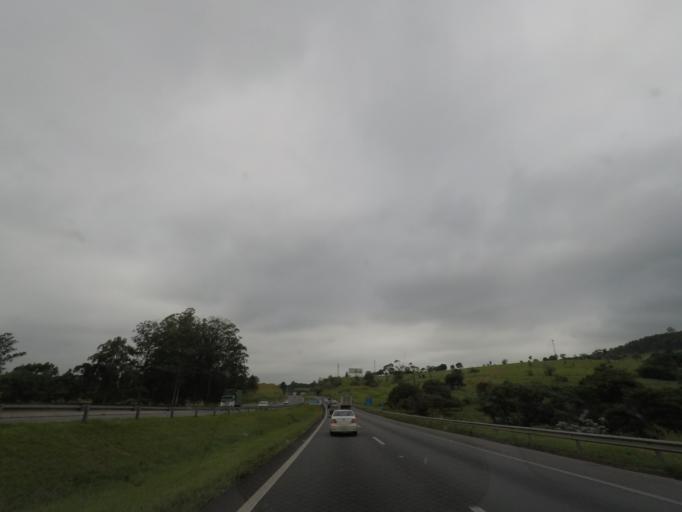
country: BR
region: Sao Paulo
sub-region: Itatiba
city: Itatiba
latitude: -23.0010
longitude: -46.7805
